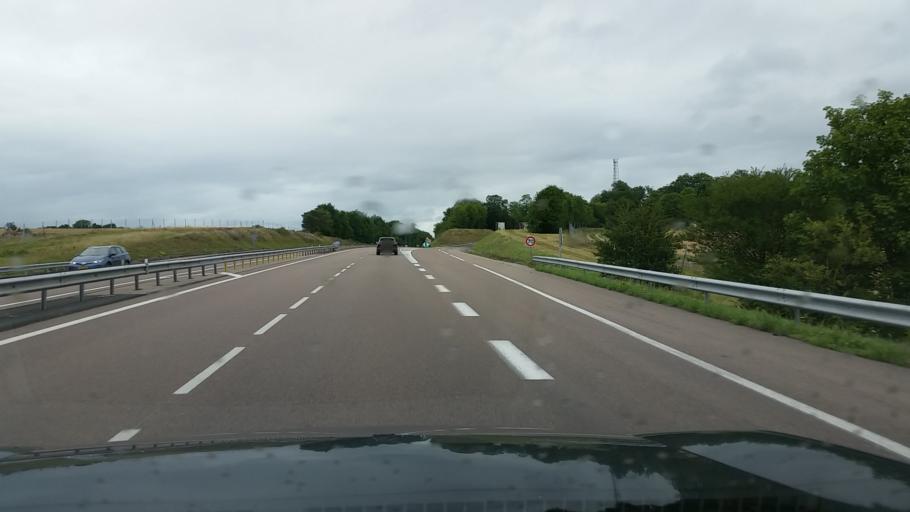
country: FR
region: Lorraine
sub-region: Departement de Meurthe-et-Moselle
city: Colombey-les-Belles
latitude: 48.4213
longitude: 5.8617
